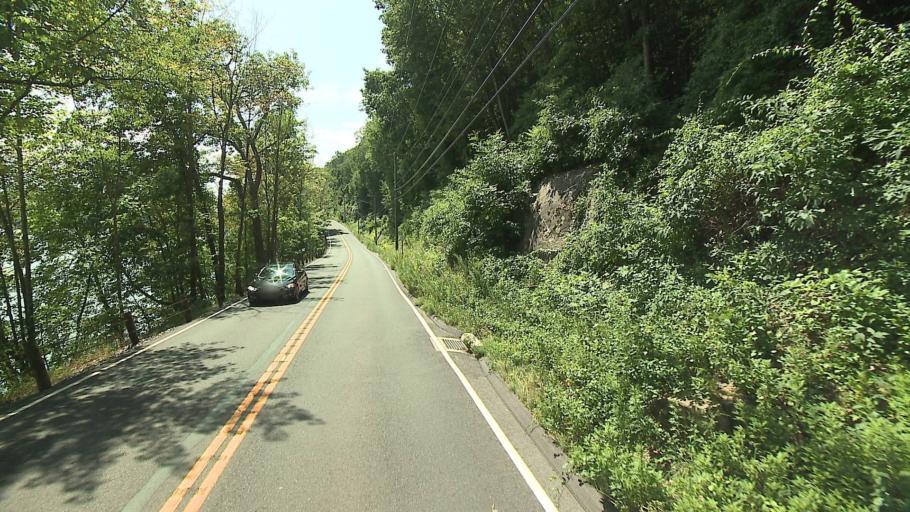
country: US
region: New York
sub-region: Putnam County
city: Putnam Lake
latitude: 41.4956
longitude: -73.4691
